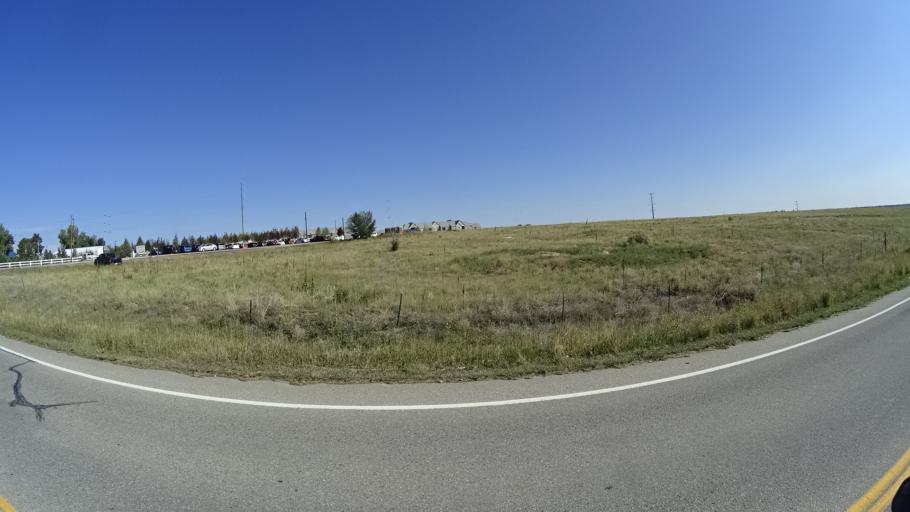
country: US
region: Colorado
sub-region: El Paso County
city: Black Forest
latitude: 38.9389
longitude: -104.7055
